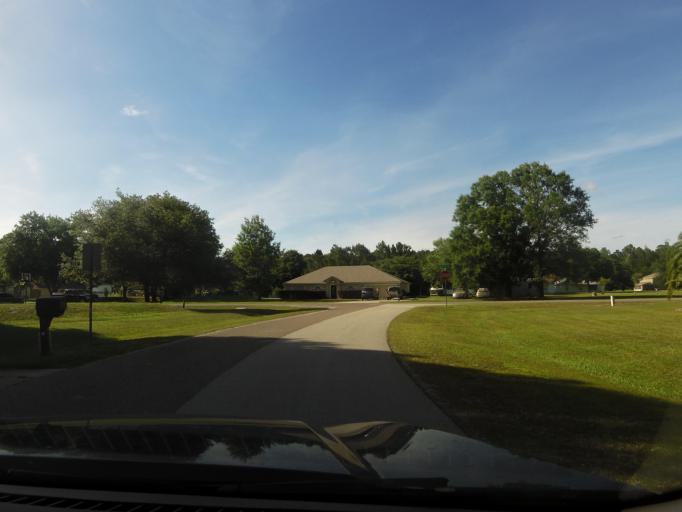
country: US
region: Florida
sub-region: Nassau County
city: Callahan
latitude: 30.5610
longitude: -81.7810
